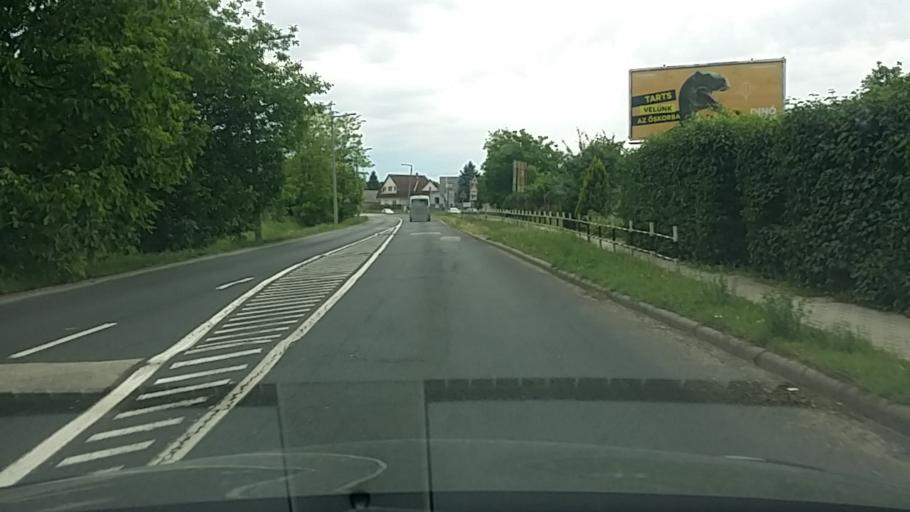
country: HU
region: Fejer
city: dunaujvaros
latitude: 46.9784
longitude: 18.9201
